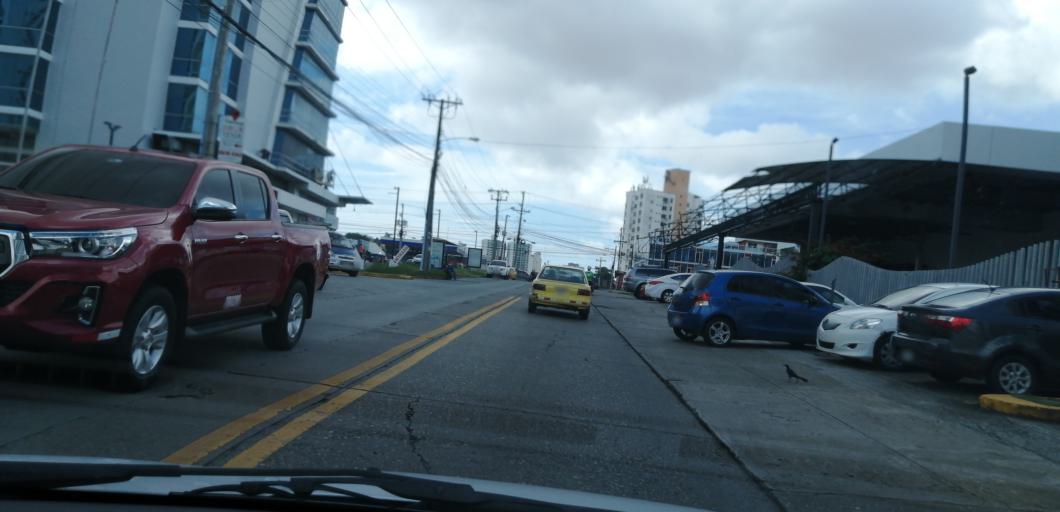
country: PA
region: Panama
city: Panama
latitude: 9.0260
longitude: -79.5237
